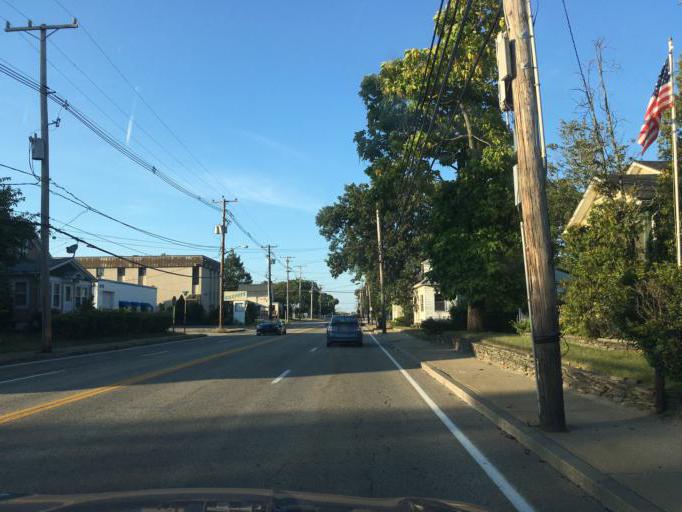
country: US
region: Rhode Island
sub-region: Providence County
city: Cranston
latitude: 41.7384
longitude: -71.4395
